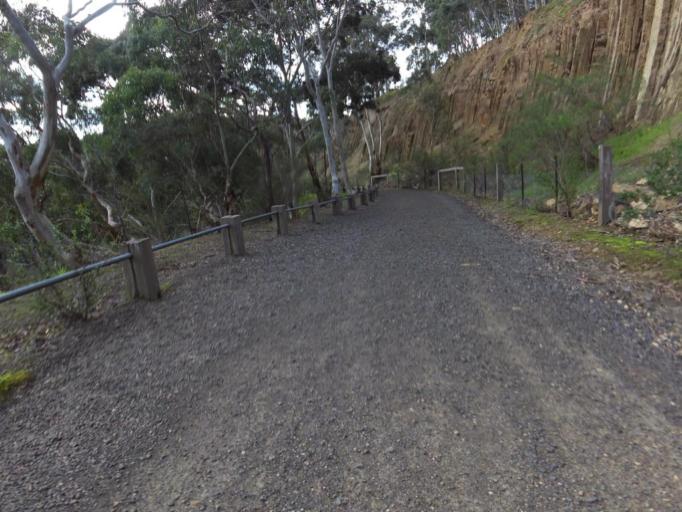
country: AU
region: Victoria
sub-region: Whittlesea
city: Mill Park
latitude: -37.6710
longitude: 145.0870
